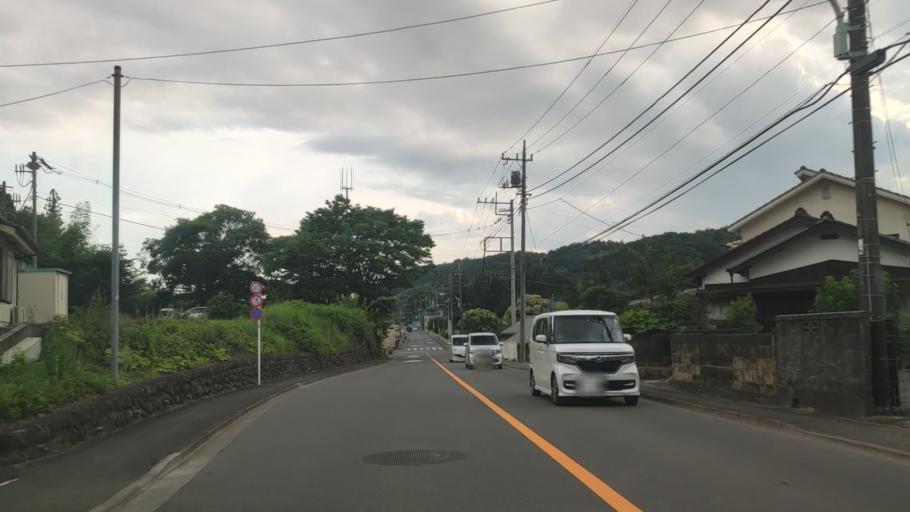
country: JP
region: Saitama
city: Hanno
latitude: 35.8297
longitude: 139.2943
